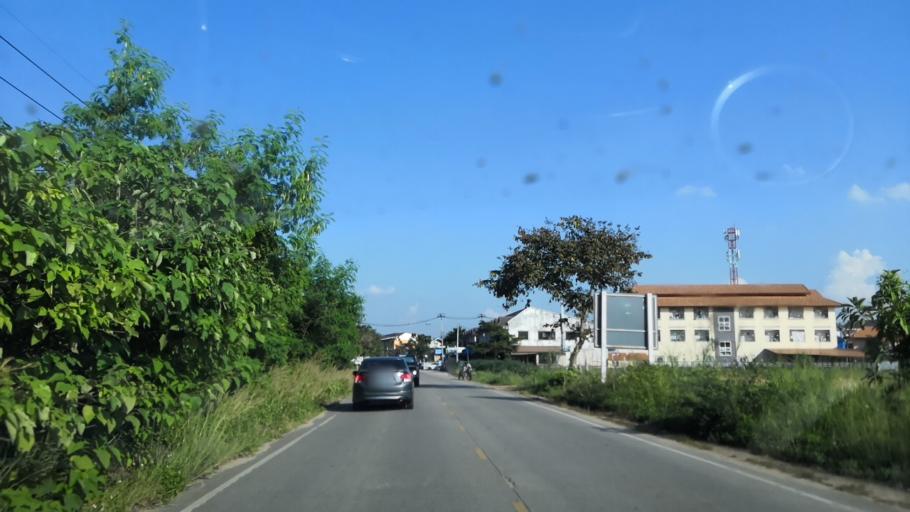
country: TH
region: Chiang Rai
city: Chiang Rai
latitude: 19.9296
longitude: 99.8595
